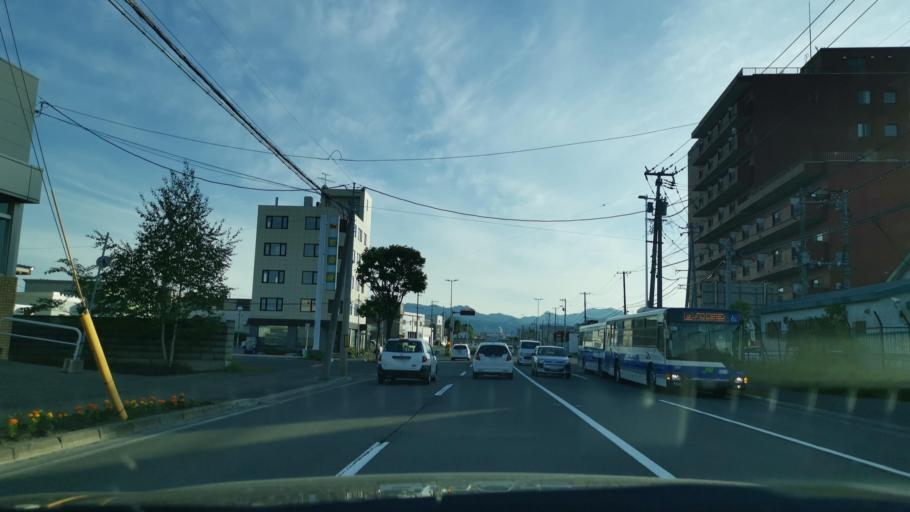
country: JP
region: Hokkaido
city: Sapporo
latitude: 43.0668
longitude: 141.3987
